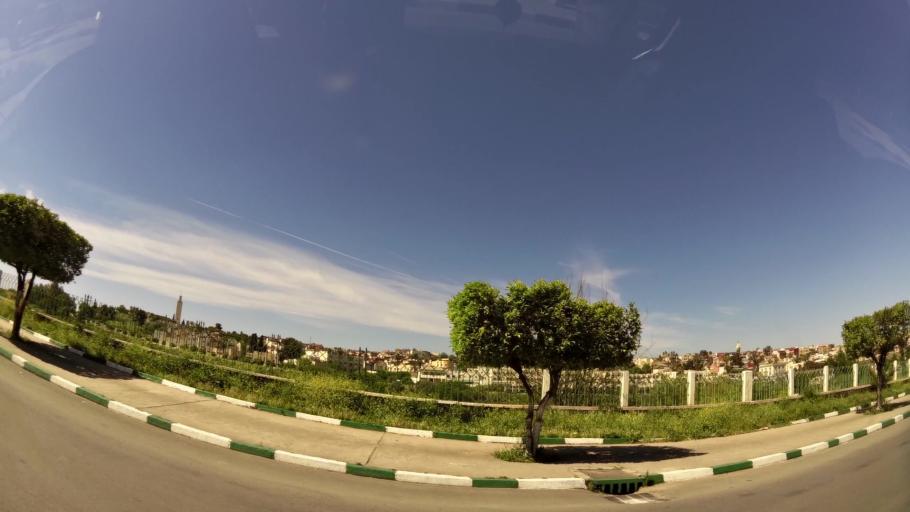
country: MA
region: Meknes-Tafilalet
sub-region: Meknes
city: Meknes
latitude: 33.8948
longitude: -5.5541
